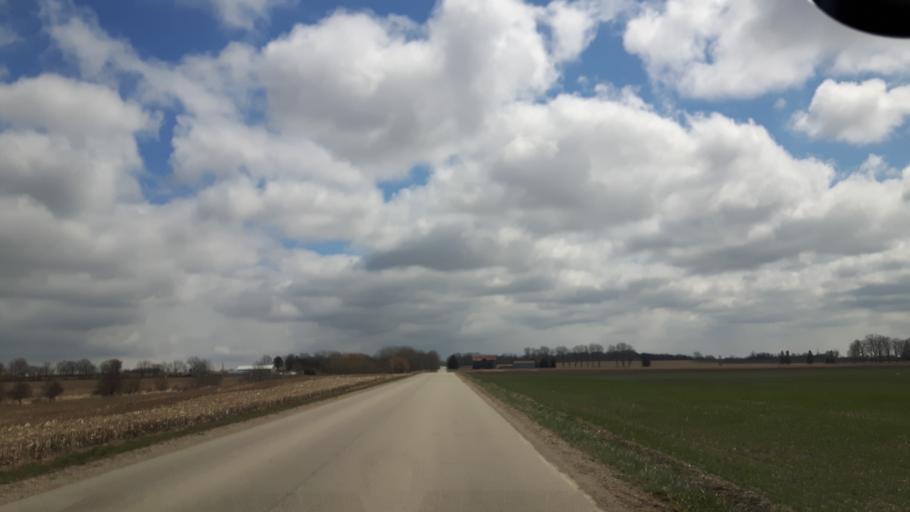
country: CA
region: Ontario
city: Goderich
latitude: 43.6984
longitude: -81.6943
